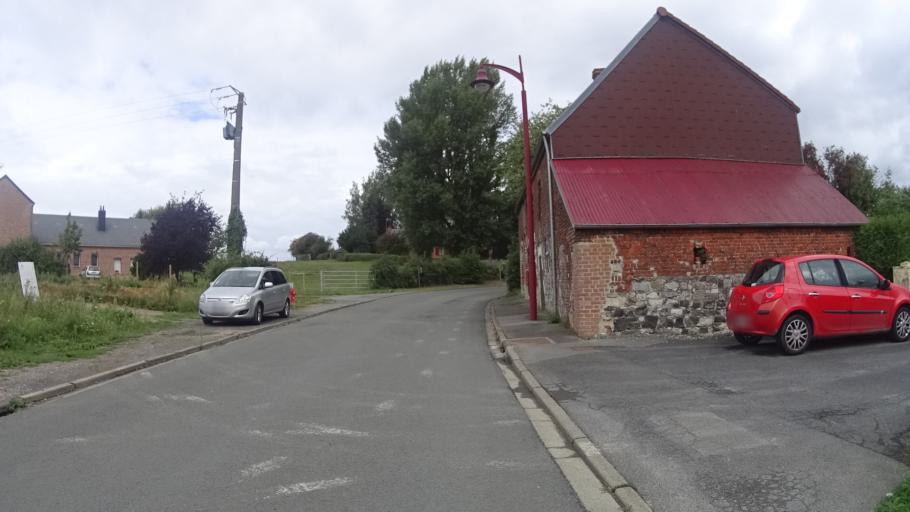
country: FR
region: Nord-Pas-de-Calais
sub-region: Departement du Nord
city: Berlaimont
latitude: 50.1806
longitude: 3.8062
